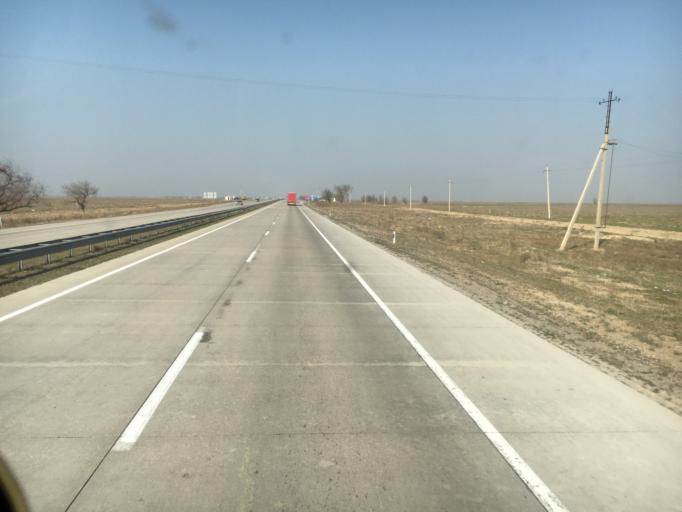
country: KZ
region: Ongtustik Qazaqstan
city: Temirlanovka
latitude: 42.8432
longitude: 69.1004
